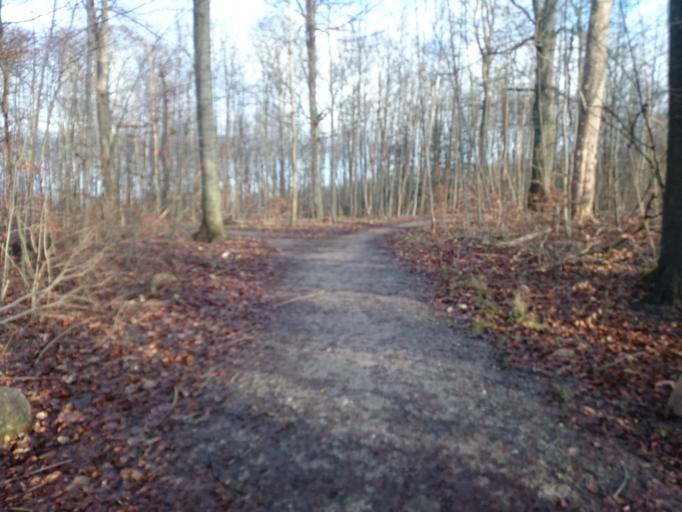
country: DK
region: Central Jutland
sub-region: Arhus Kommune
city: Stavtrup
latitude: 56.1311
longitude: 10.1424
